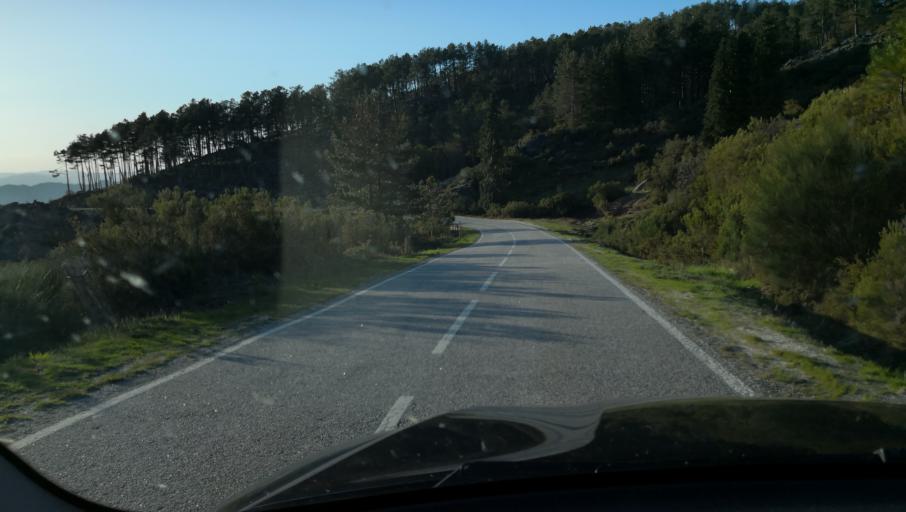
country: PT
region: Vila Real
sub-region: Vila Real
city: Vila Real
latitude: 41.3862
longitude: -7.8234
